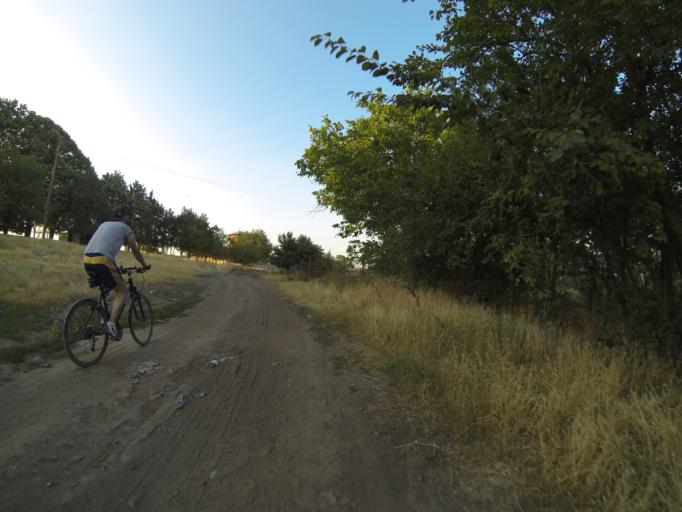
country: RO
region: Dolj
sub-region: Comuna Segarcea
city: Segarcea
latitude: 44.0809
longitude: 23.7249
